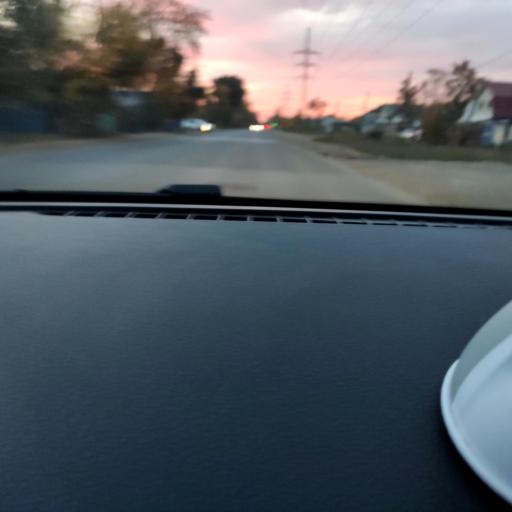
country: RU
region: Samara
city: Samara
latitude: 53.1327
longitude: 50.1323
